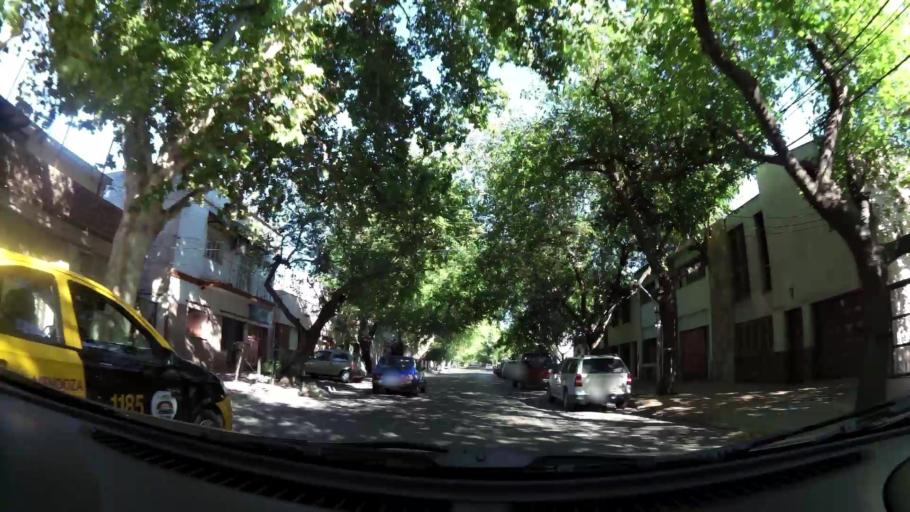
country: AR
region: Mendoza
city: Mendoza
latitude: -32.8779
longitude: -68.8521
